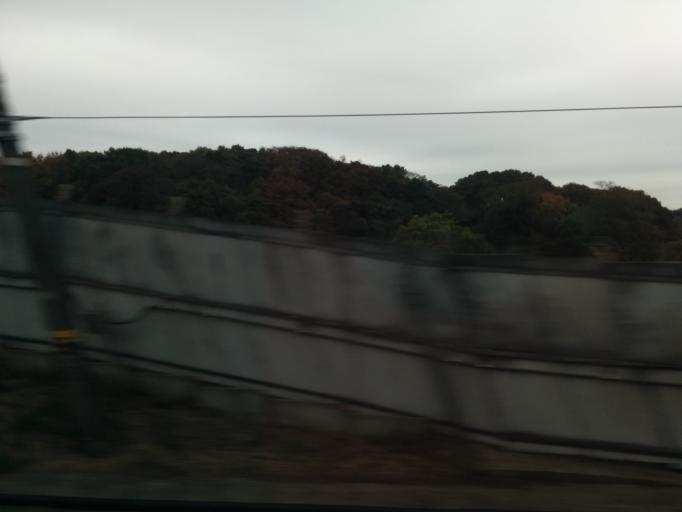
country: JP
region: Kanagawa
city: Yokohama
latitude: 35.4834
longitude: 139.5827
